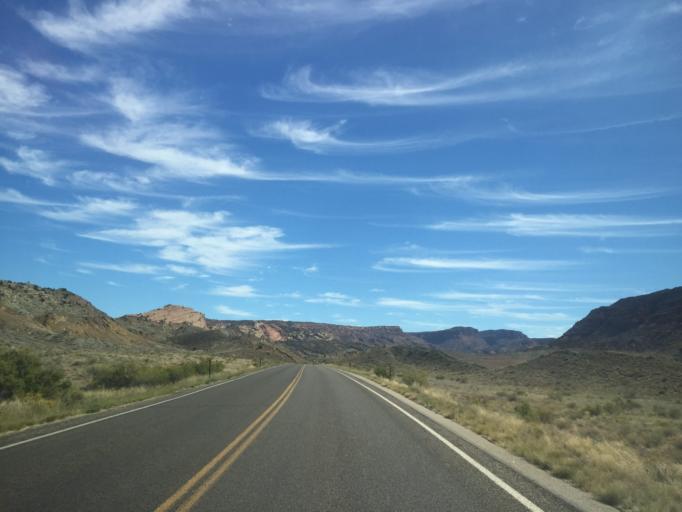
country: US
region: Utah
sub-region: Grand County
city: Moab
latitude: 38.7330
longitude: -109.5123
